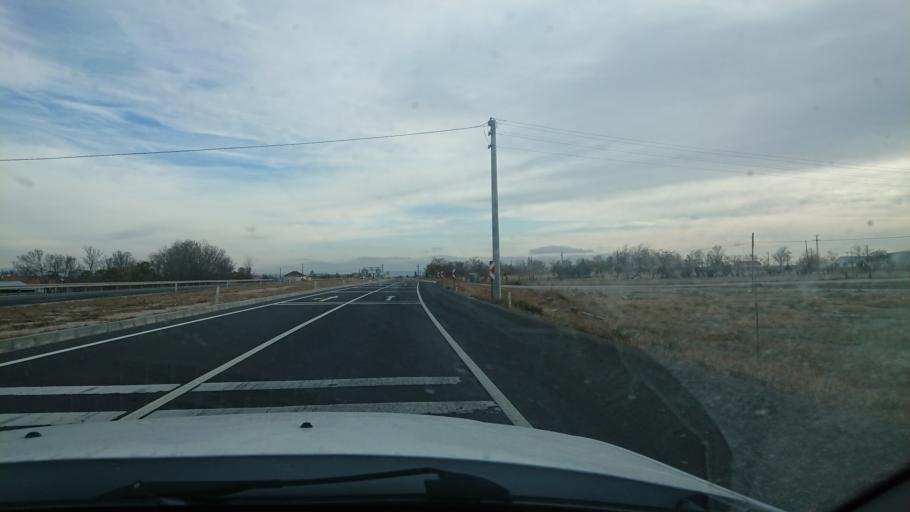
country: TR
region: Aksaray
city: Yesilova
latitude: 38.3245
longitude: 33.8804
